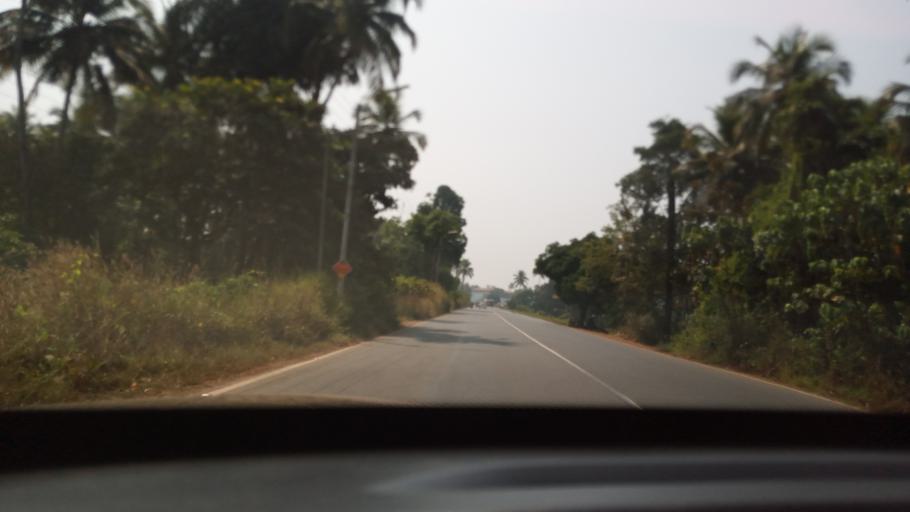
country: IN
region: Goa
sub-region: South Goa
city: Sancoale
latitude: 15.3390
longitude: 73.9278
